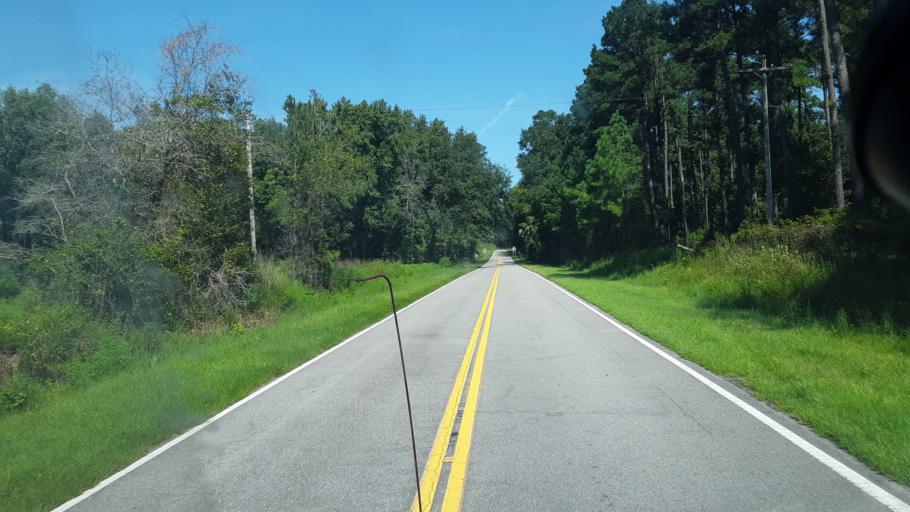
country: US
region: South Carolina
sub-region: Hampton County
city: Varnville
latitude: 32.9002
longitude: -81.0060
